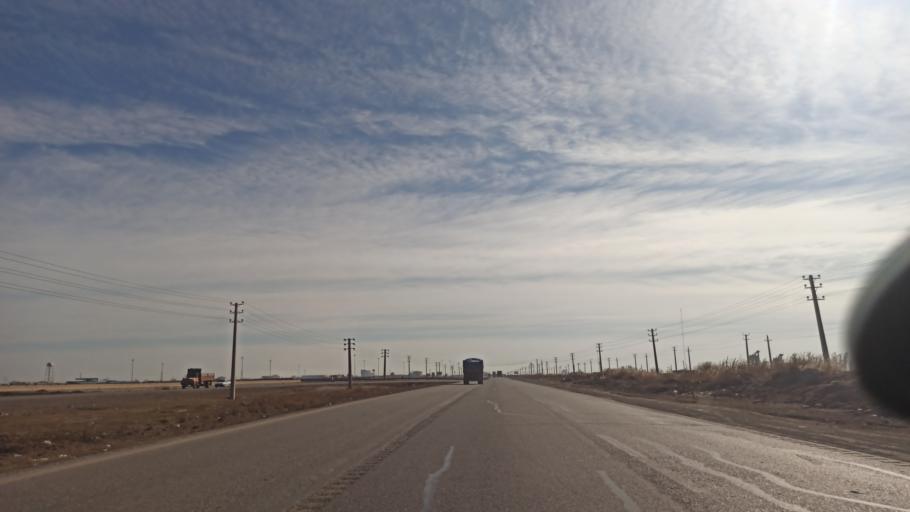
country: IR
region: Qazvin
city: Alvand
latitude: 36.1185
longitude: 50.0386
